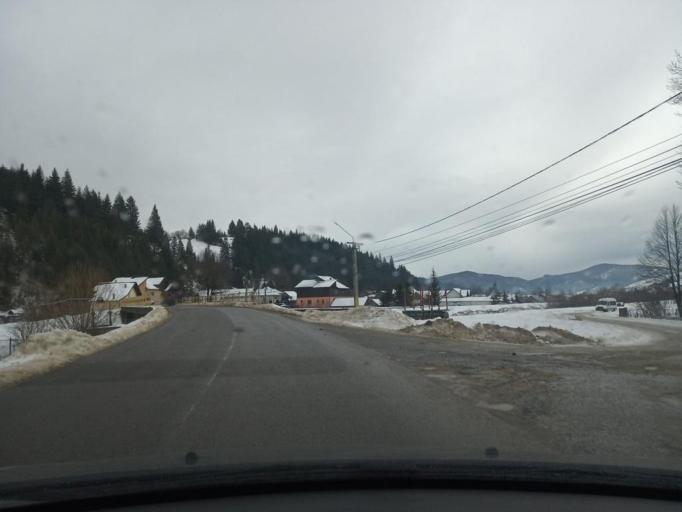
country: RO
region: Suceava
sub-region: Comuna Manastirea Humorului
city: Manastirea Humorului
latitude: 47.5904
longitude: 25.8664
